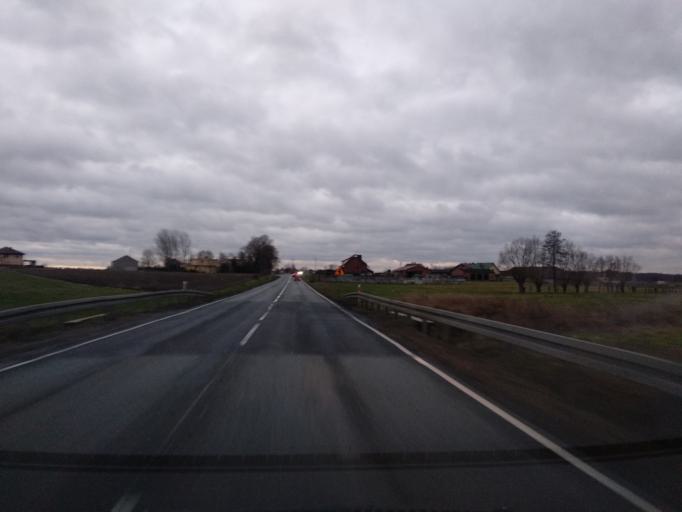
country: PL
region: Greater Poland Voivodeship
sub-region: Powiat koninski
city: Rychwal
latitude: 52.1296
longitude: 18.1797
